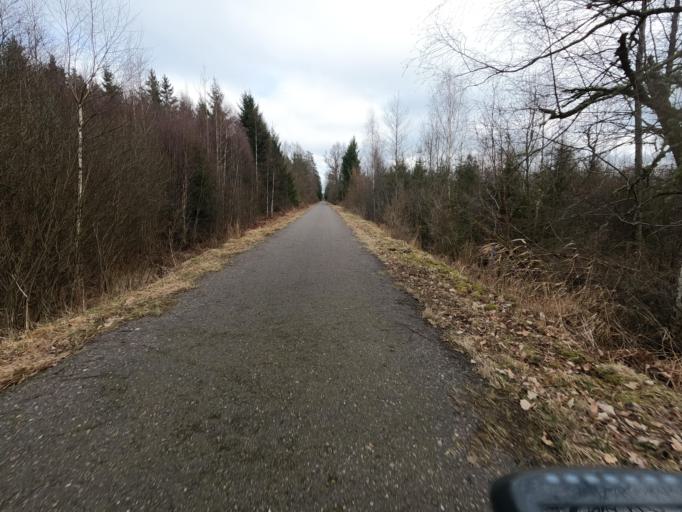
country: SE
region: Joenkoeping
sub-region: Varnamo Kommun
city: Rydaholm
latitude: 56.8483
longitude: 14.2069
